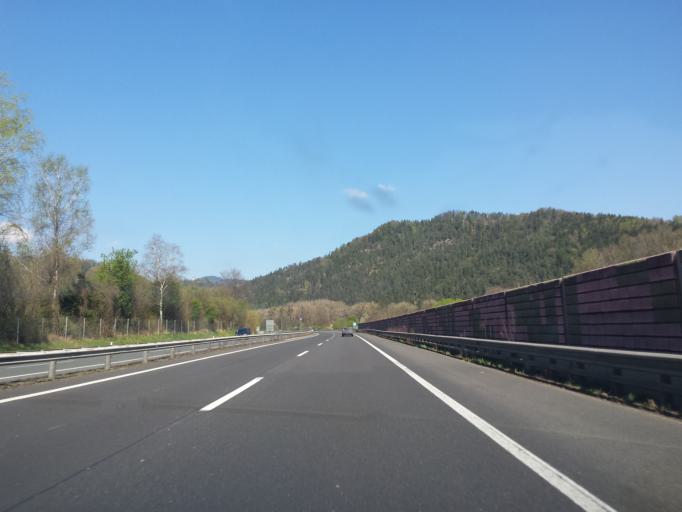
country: AT
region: Styria
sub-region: Politischer Bezirk Graz-Umgebung
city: Deutschfeistritz
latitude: 47.2144
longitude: 15.3063
